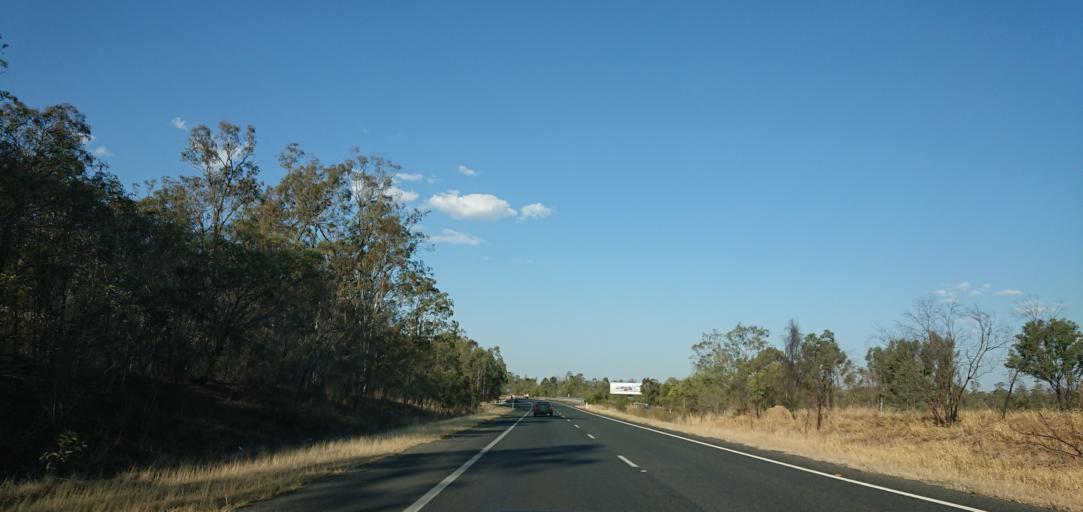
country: AU
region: Queensland
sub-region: Lockyer Valley
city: Gatton
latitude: -27.5515
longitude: 152.2103
